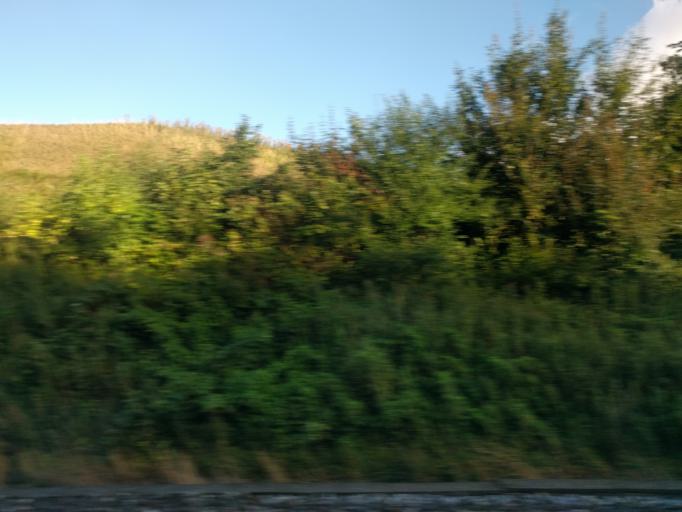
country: DK
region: Zealand
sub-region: Slagelse Kommune
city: Slagelse
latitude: 55.4047
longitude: 11.3189
